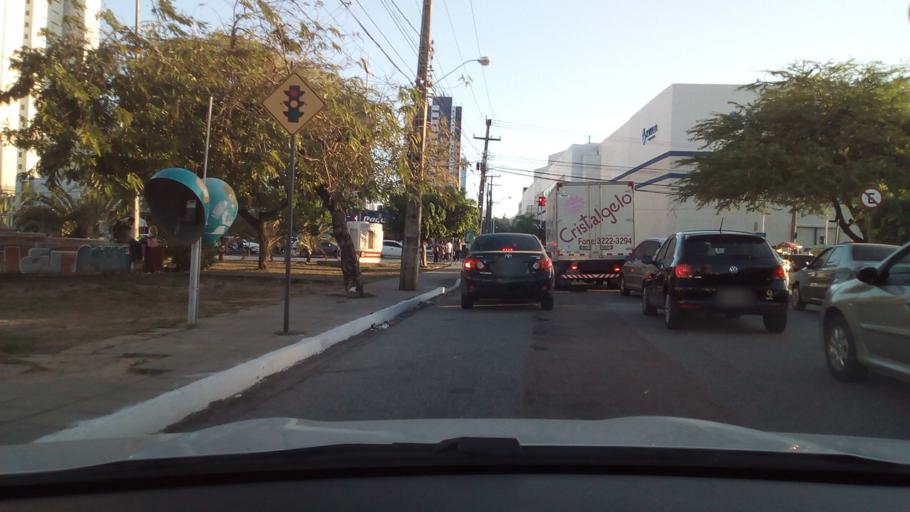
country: BR
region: Paraiba
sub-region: Joao Pessoa
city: Joao Pessoa
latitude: -7.0973
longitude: -34.8443
